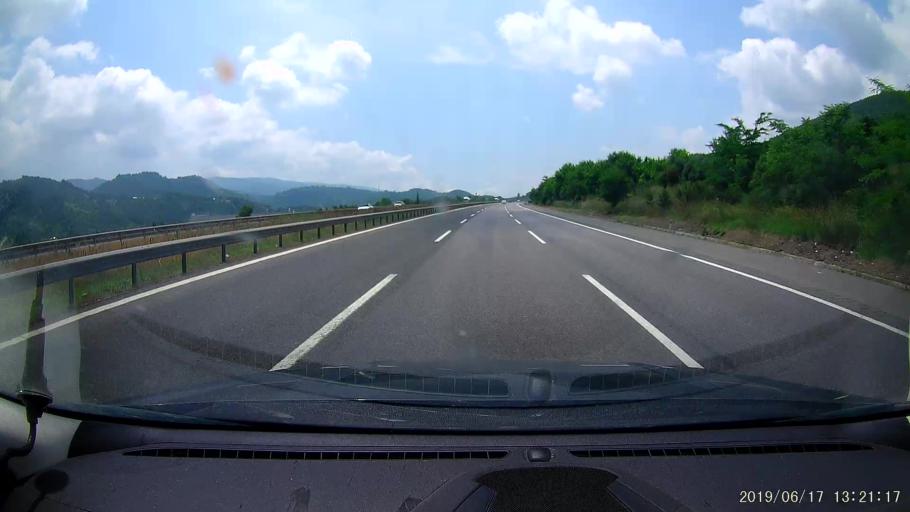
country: TR
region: Duzce
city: Gumusova
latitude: 40.8346
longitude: 30.9384
